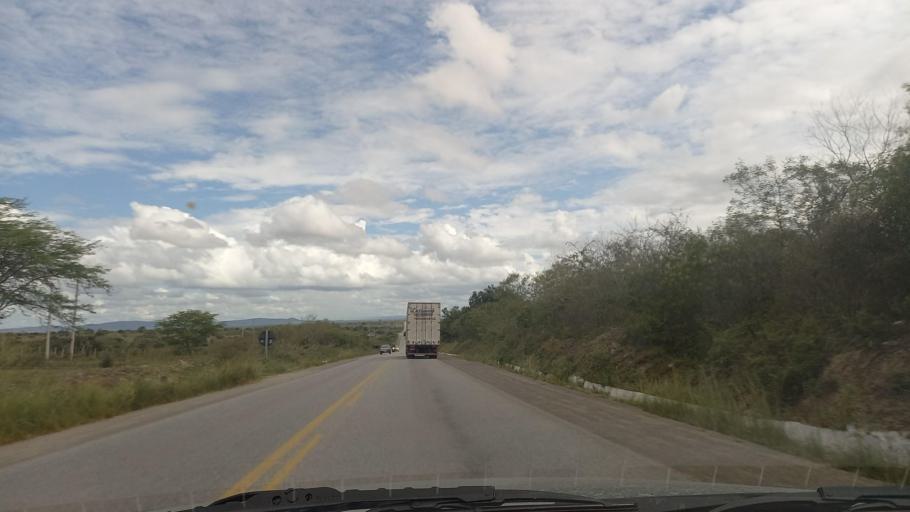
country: BR
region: Pernambuco
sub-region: Cachoeirinha
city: Cachoeirinha
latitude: -8.3838
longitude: -36.1745
